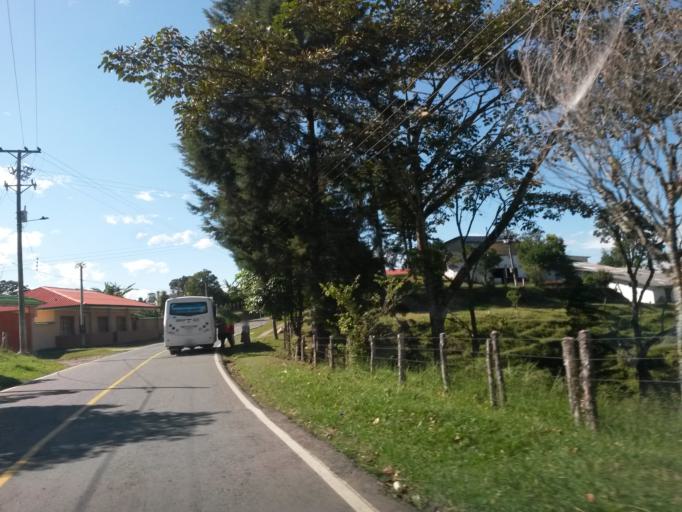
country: CO
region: Cauca
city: Morales
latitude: 2.7480
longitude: -76.6235
